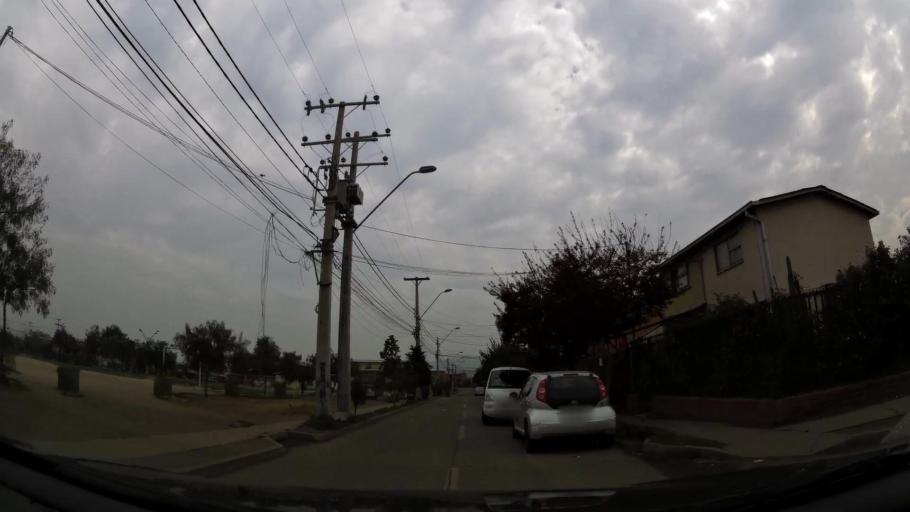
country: CL
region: Santiago Metropolitan
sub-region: Provincia de Chacabuco
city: Chicureo Abajo
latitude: -33.1901
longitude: -70.6692
